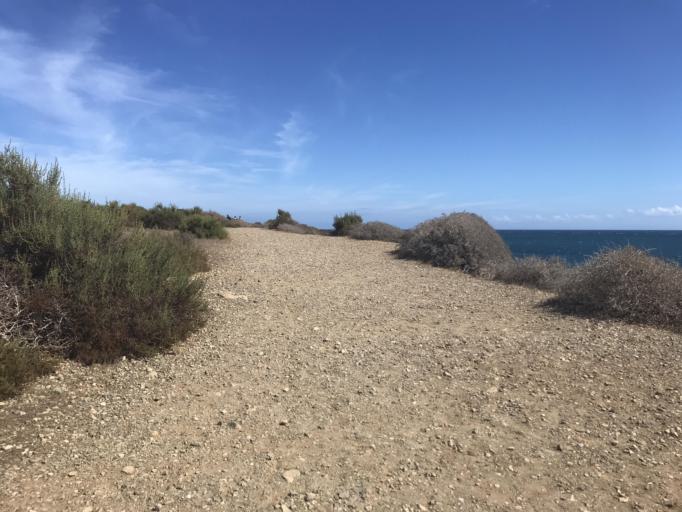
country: ES
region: Valencia
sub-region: Provincia de Alicante
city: Santa Pola
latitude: 38.1628
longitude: -0.4701
